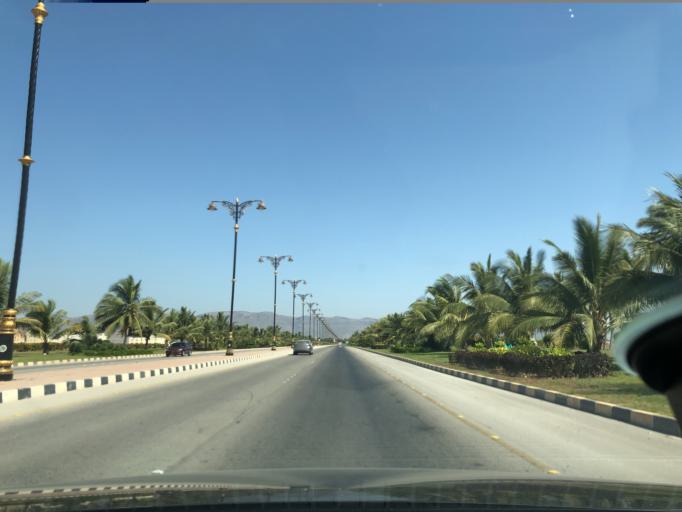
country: OM
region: Zufar
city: Salalah
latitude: 17.0443
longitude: 54.2077
